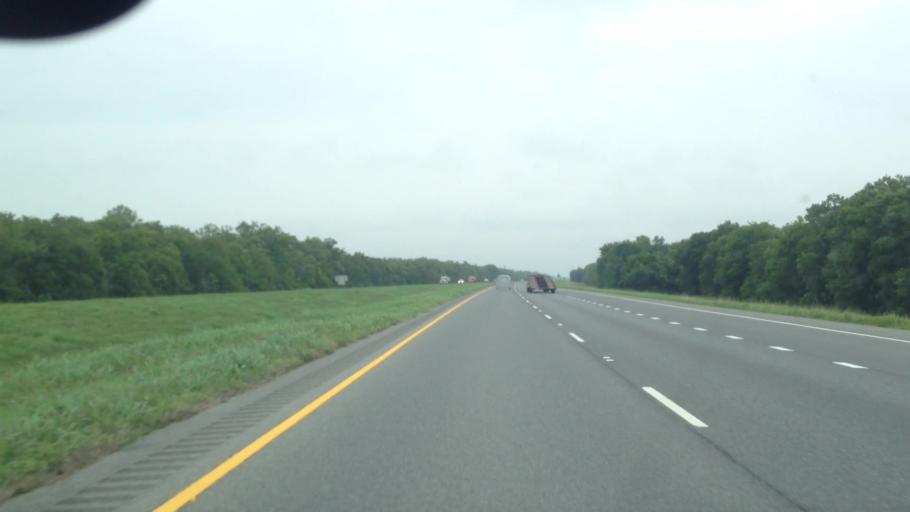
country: US
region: Louisiana
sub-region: Evangeline Parish
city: Ville Platte
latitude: 30.7280
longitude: -92.1241
